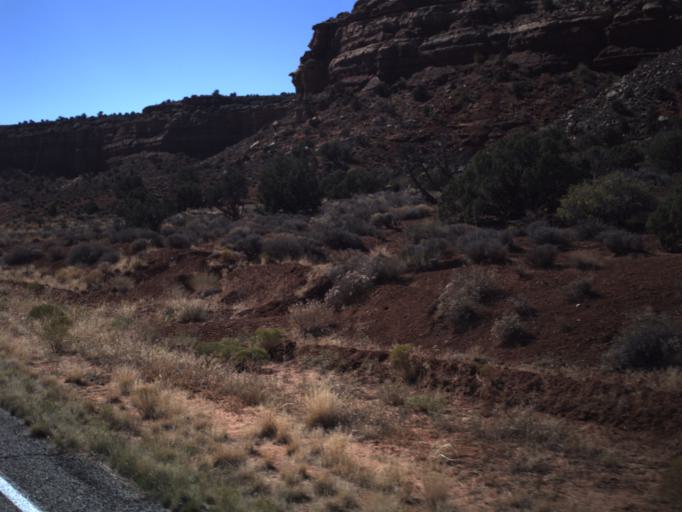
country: US
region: Utah
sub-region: San Juan County
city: Blanding
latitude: 37.7287
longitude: -110.2497
